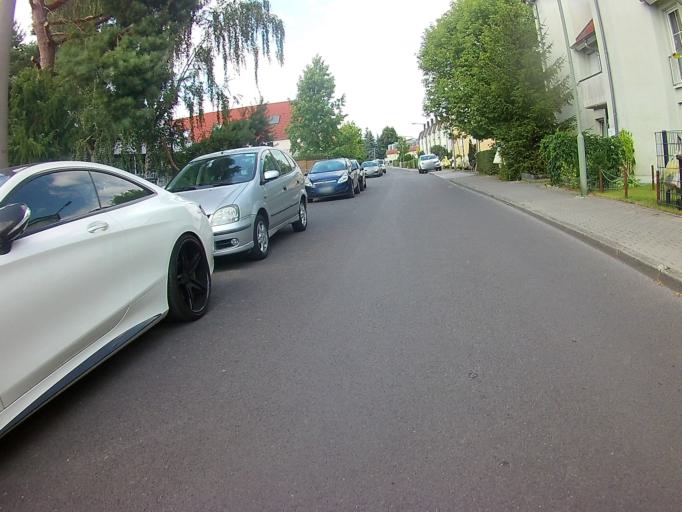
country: DE
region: Berlin
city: Bohnsdorf
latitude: 52.3971
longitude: 13.5648
